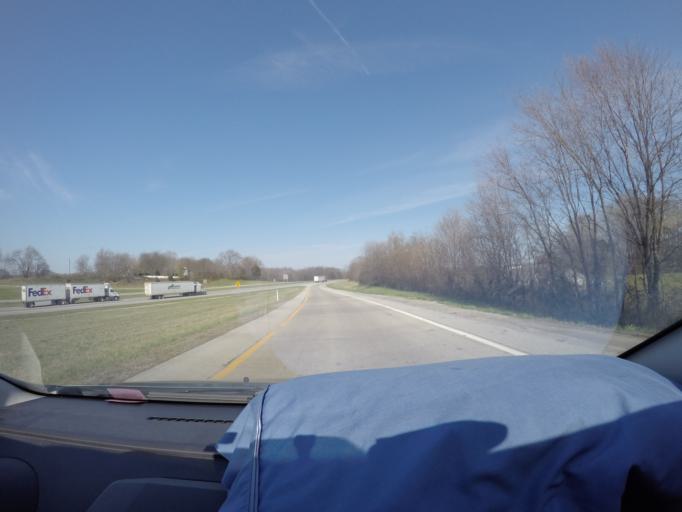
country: US
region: Tennessee
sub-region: Marion County
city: Monteagle
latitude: 35.3012
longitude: -85.9029
